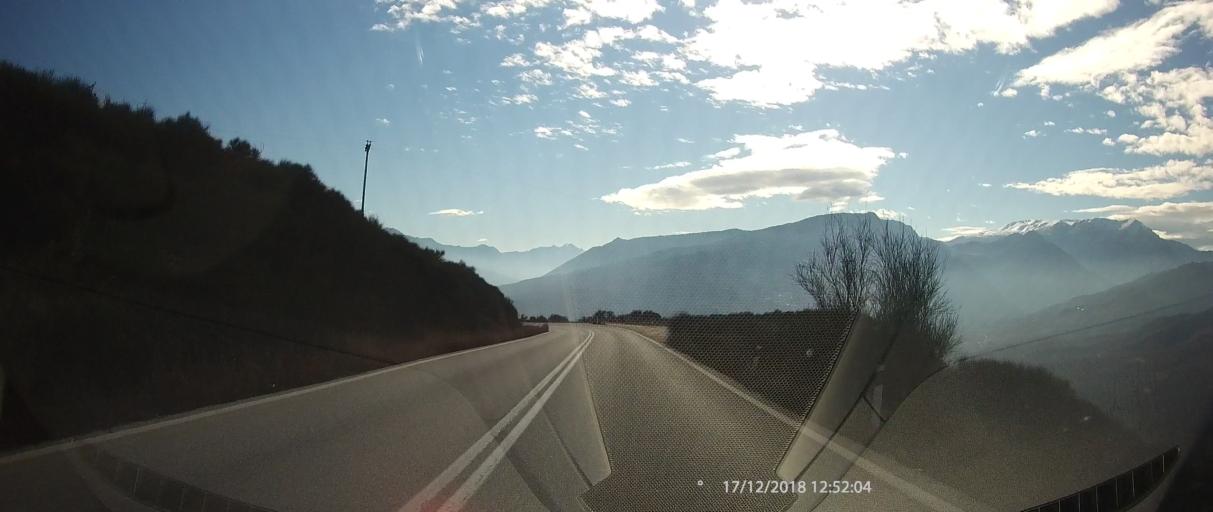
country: GR
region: Thessaly
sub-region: Trikala
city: Kastraki
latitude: 39.7600
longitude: 21.4740
